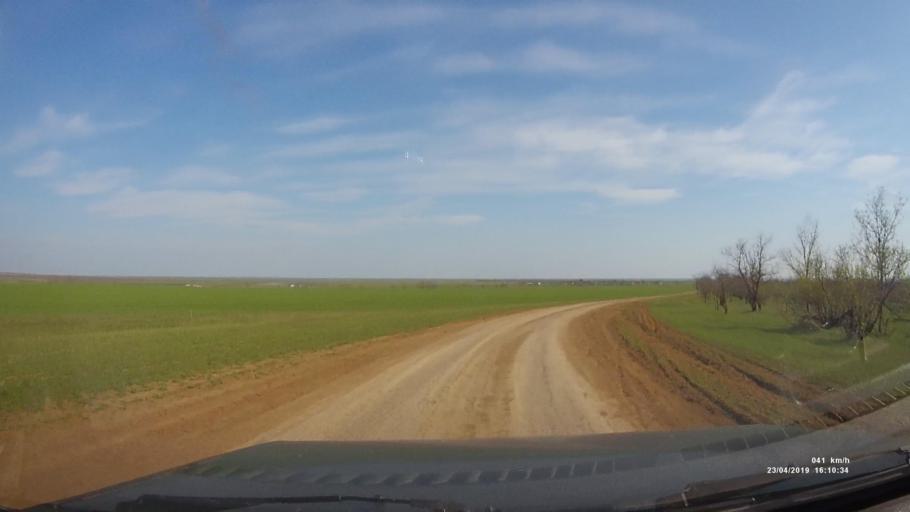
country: RU
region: Rostov
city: Remontnoye
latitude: 46.4811
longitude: 43.1229
